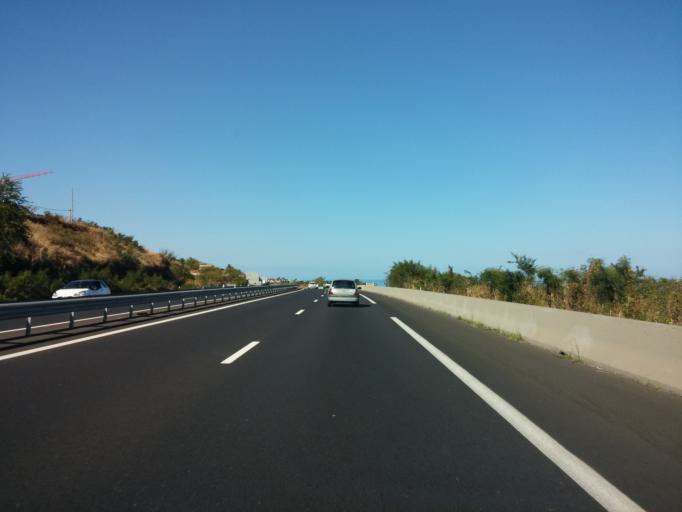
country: RE
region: Reunion
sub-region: Reunion
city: Saint-Leu
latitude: -21.1906
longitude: 55.2965
